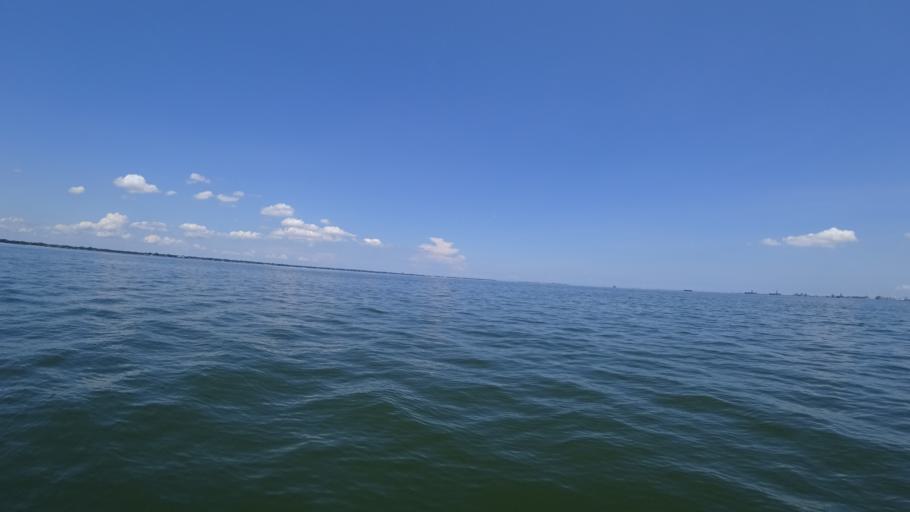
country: US
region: Virginia
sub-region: City of Newport News
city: Newport News
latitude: 36.9500
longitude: -76.3885
